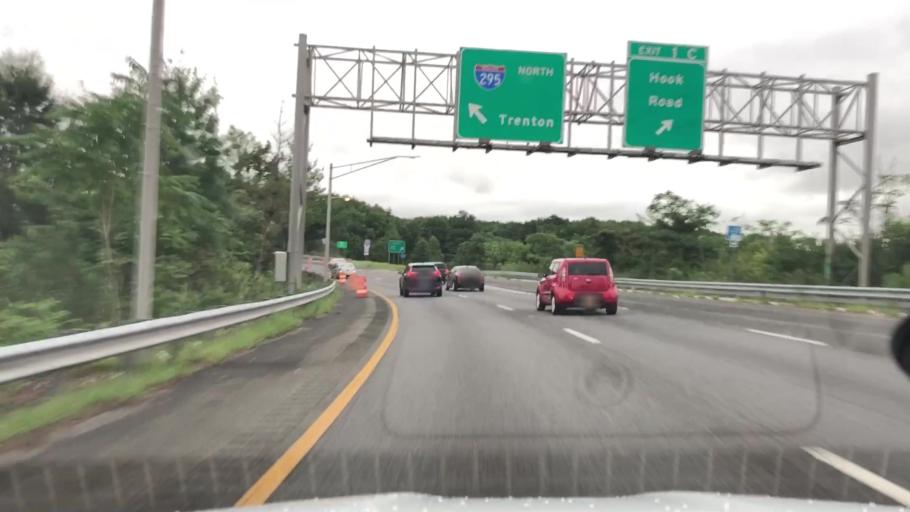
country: US
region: New Jersey
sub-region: Salem County
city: Pennsville
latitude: 39.6773
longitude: -75.4888
